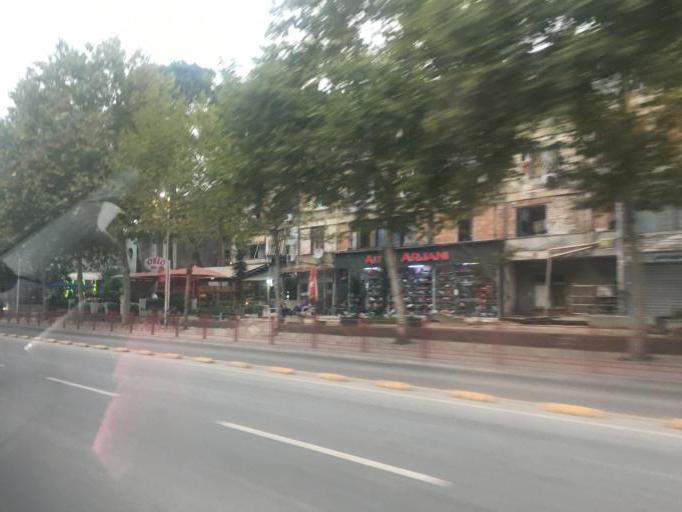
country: AL
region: Tirane
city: Tirana
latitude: 41.3346
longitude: 19.7999
